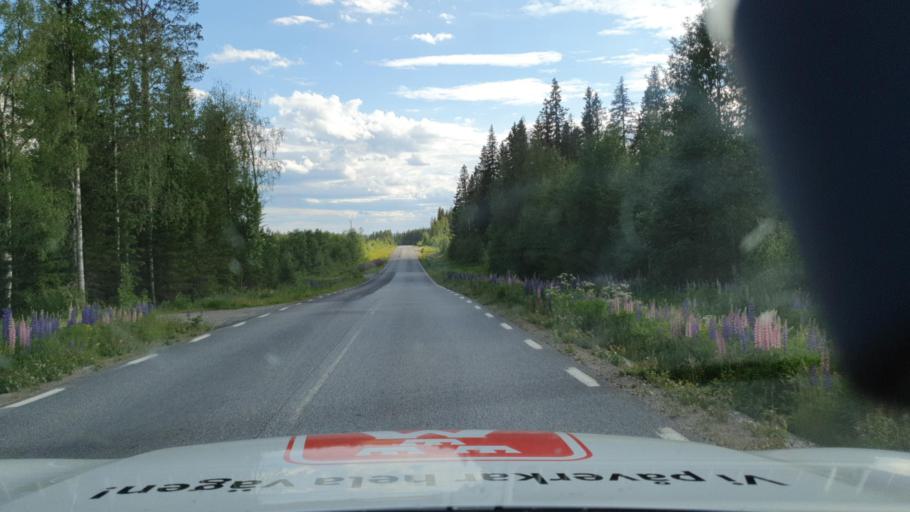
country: SE
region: Vaesterbotten
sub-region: Skelleftea Kommun
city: Langsele
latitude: 64.5605
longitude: 19.9283
